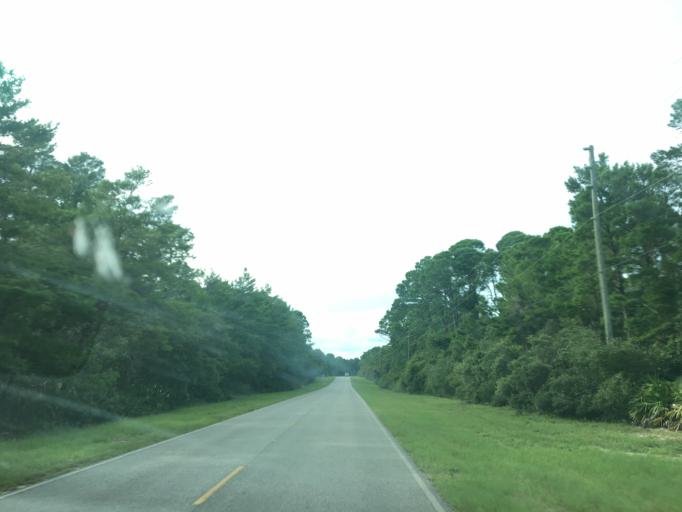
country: US
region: Florida
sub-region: Wakulla County
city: Crawfordville
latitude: 29.9237
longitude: -84.3744
